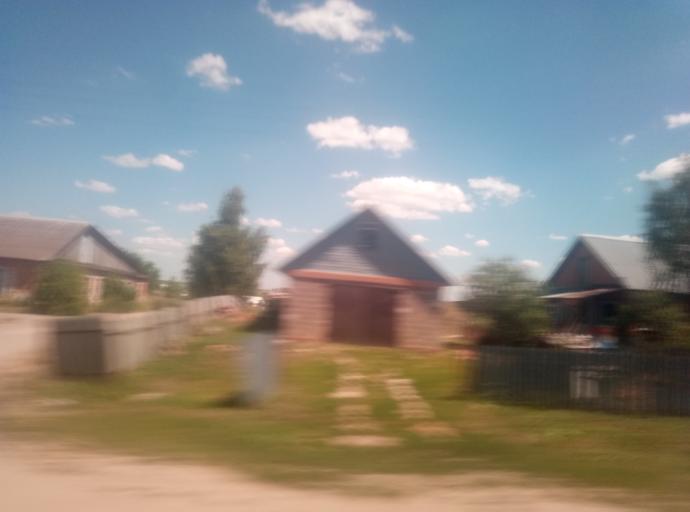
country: RU
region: Tula
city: Kireyevsk
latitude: 53.9671
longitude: 37.9347
